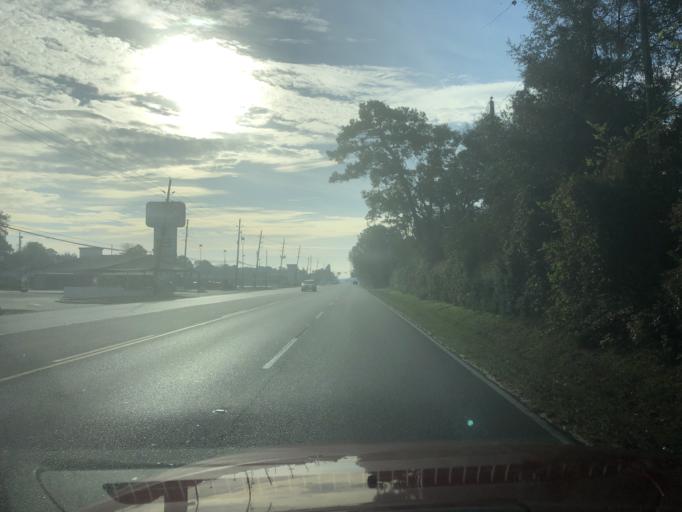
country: US
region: Texas
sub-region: Harris County
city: Spring
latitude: 30.0165
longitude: -95.4708
